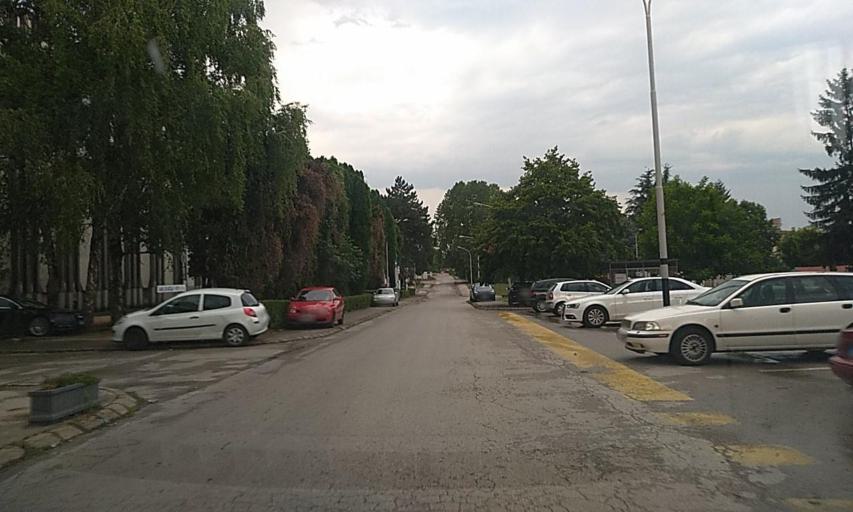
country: RS
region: Central Serbia
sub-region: Nisavski Okrug
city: Nis
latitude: 43.3060
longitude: 21.9481
